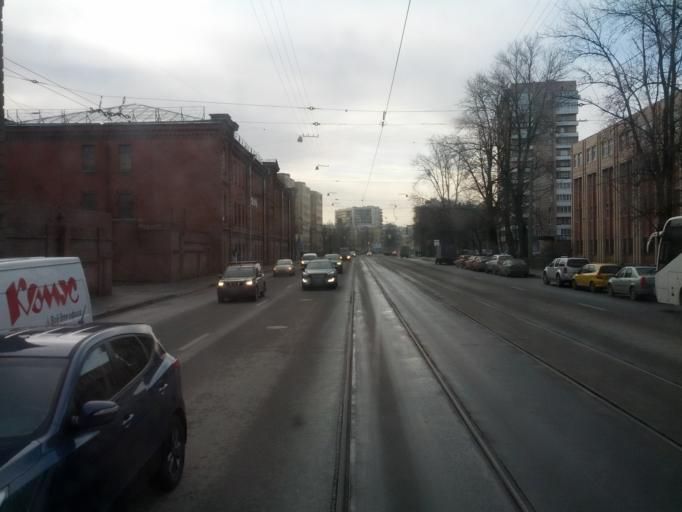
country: RU
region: St.-Petersburg
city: Centralniy
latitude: 59.9393
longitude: 30.4085
